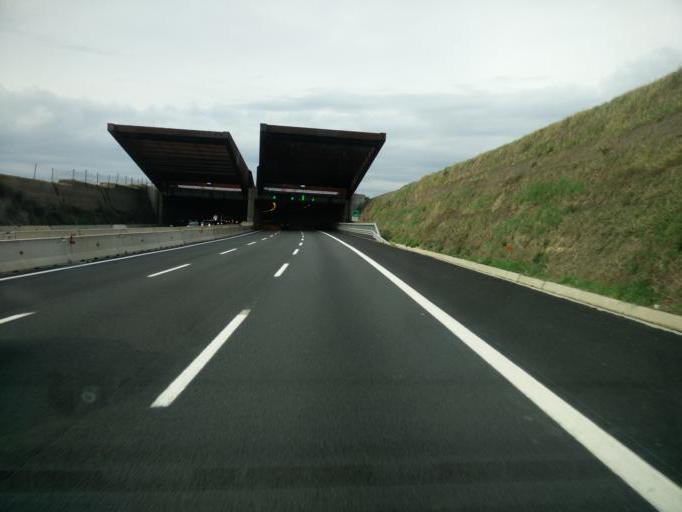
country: IT
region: Tuscany
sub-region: Province of Florence
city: Scandicci
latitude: 43.7617
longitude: 11.1697
